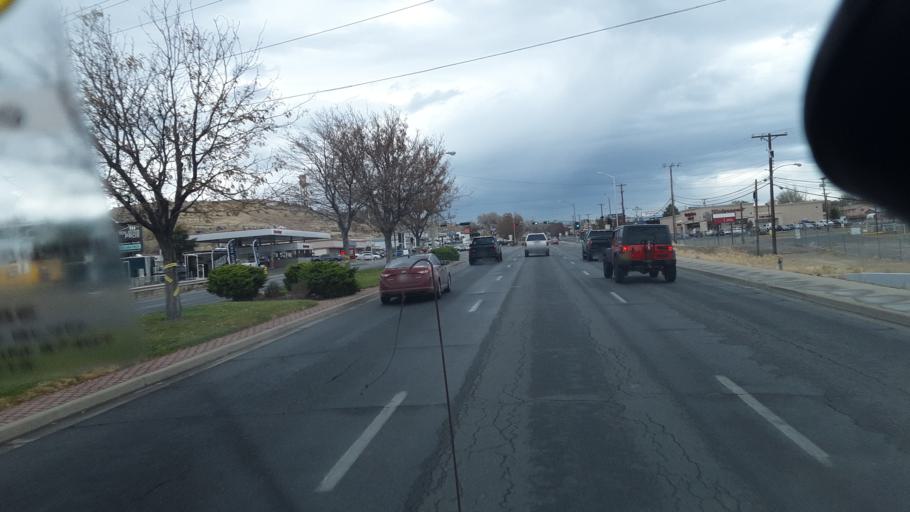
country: US
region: New Mexico
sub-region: San Juan County
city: Farmington
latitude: 36.7573
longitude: -108.1562
